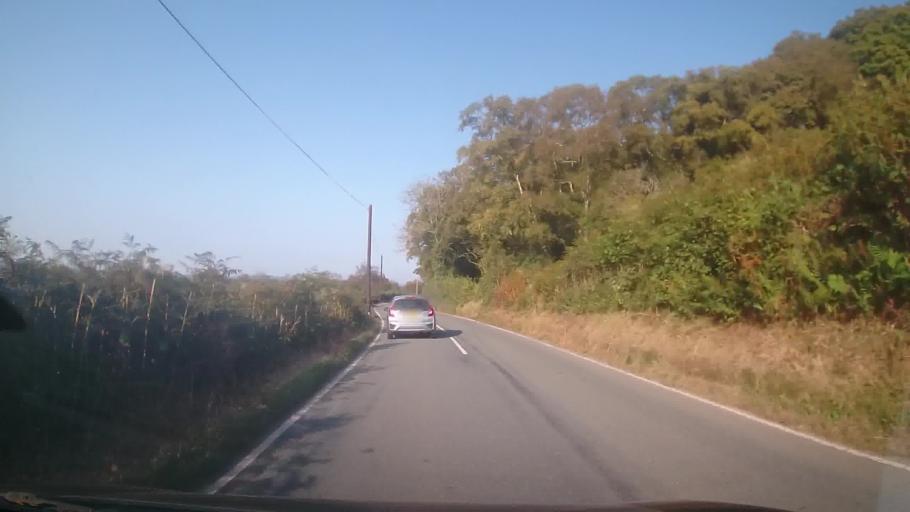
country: GB
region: Wales
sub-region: County of Ceredigion
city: Lledrod
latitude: 52.2371
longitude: -3.9269
